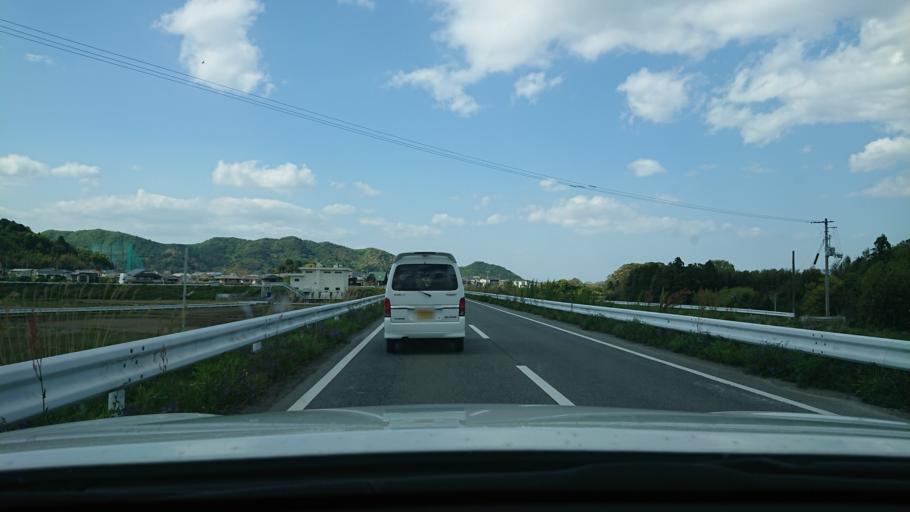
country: JP
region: Tokushima
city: Komatsushimacho
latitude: 33.9976
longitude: 134.5476
